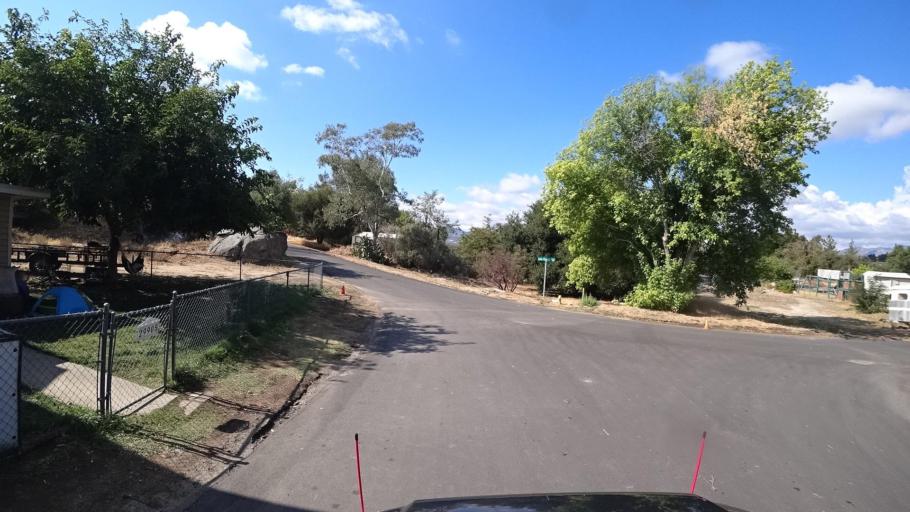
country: US
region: California
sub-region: San Diego County
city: Campo
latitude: 32.6784
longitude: -116.5039
